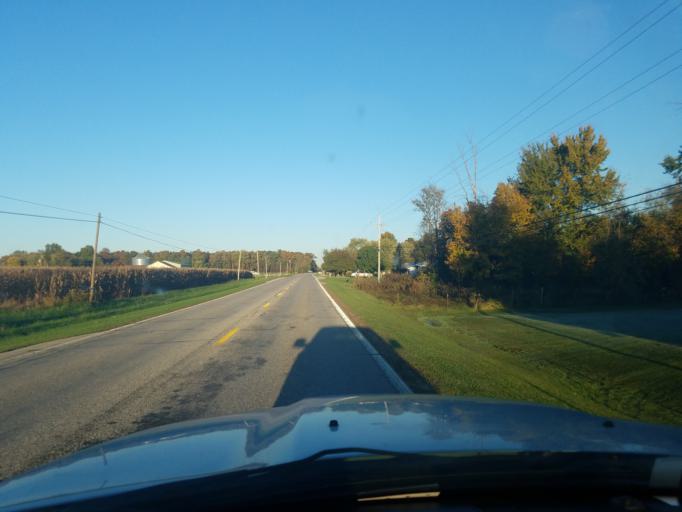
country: US
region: Indiana
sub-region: Washington County
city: New Pekin
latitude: 38.3980
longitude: -86.0773
